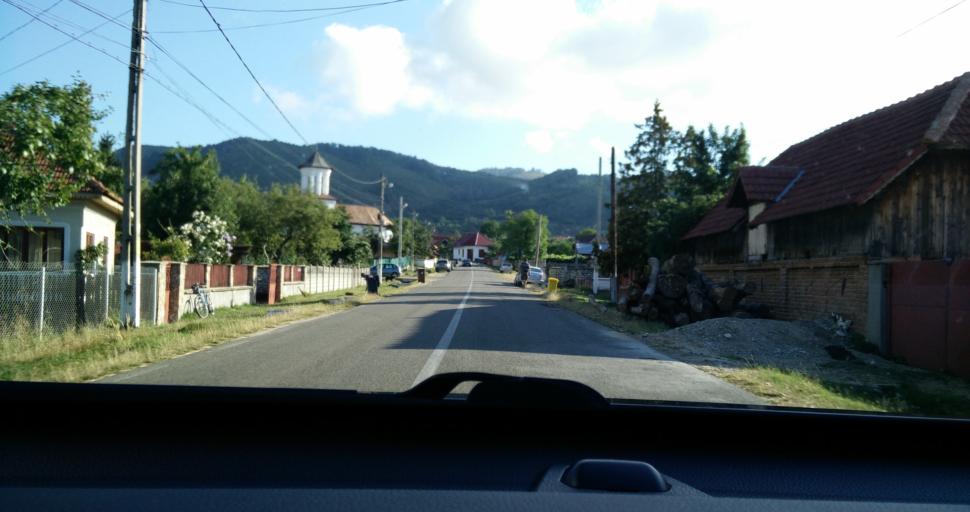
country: RO
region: Gorj
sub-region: Comuna Baia de Fier
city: Baia de Fier
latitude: 45.1769
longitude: 23.7560
